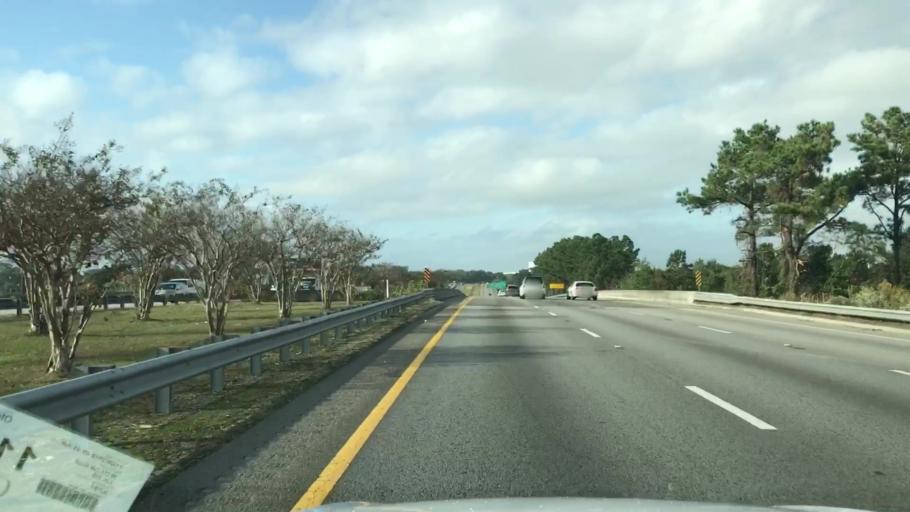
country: US
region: South Carolina
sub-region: Charleston County
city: North Charleston
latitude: 32.8563
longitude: -80.0222
